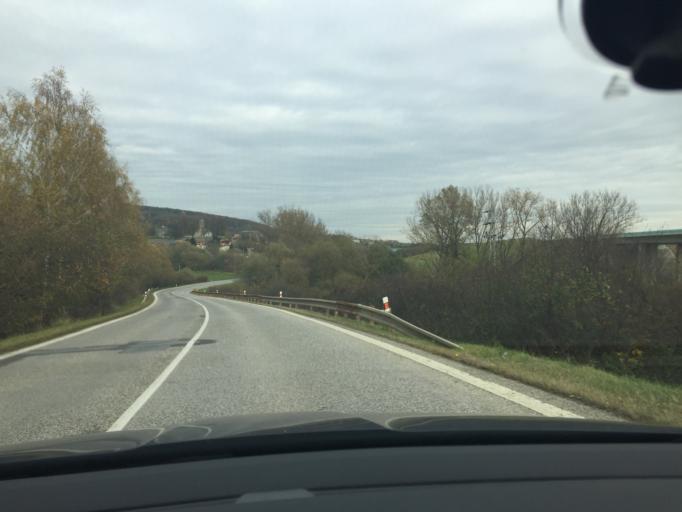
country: SK
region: Presovsky
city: Sabinov
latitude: 49.0051
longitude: 21.1165
